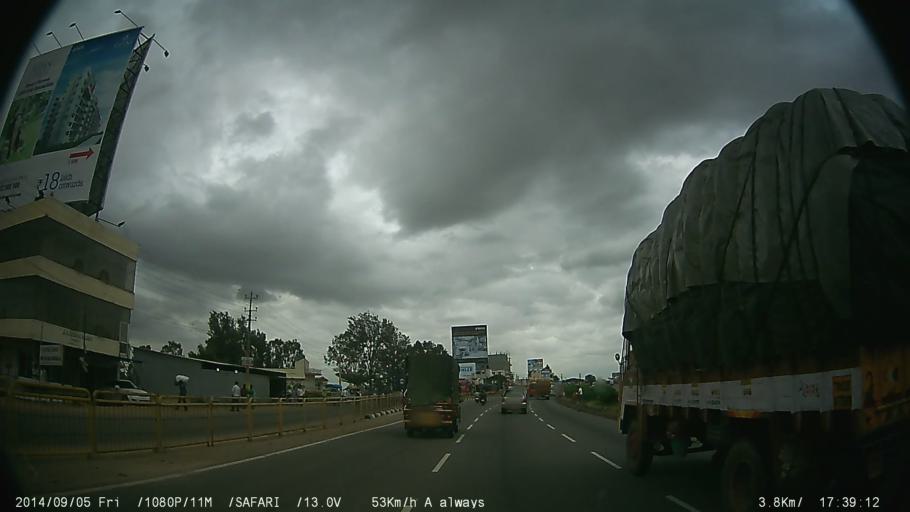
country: IN
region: Karnataka
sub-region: Bangalore Urban
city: Anekal
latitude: 12.7919
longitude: 77.7296
